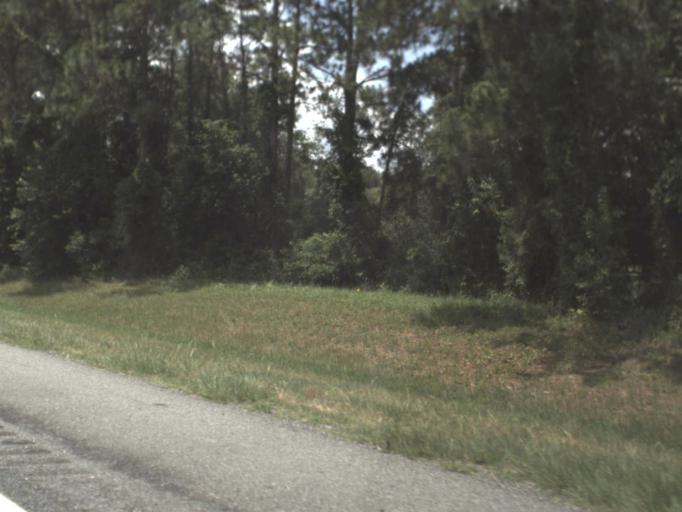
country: US
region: Florida
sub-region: Suwannee County
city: Wellborn
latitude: 30.2423
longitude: -82.7408
